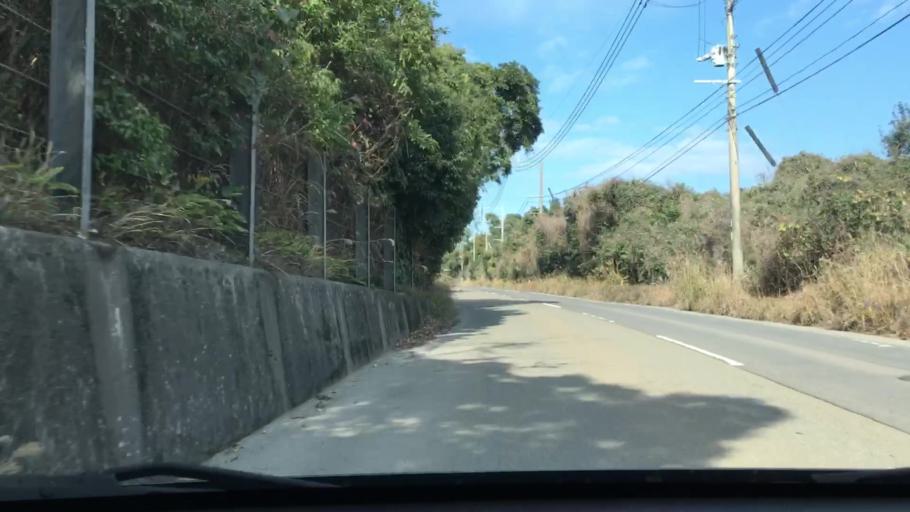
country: JP
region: Kagoshima
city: Tarumizu
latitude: 31.5720
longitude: 130.7097
